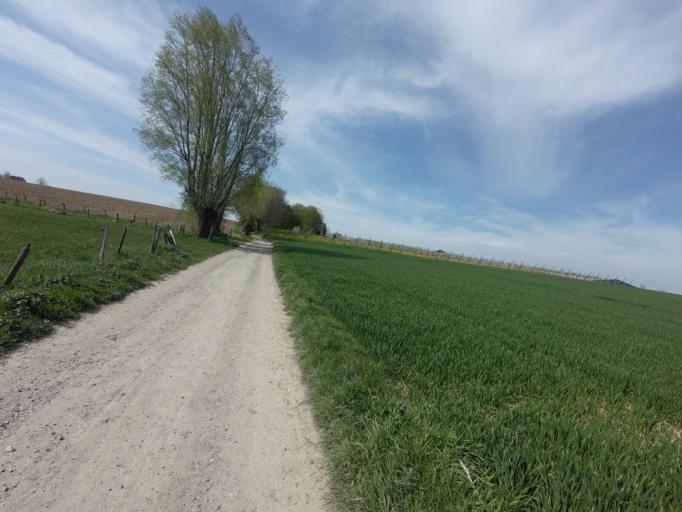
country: NL
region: Limburg
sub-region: Eijsden-Margraten
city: Margraten
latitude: 50.7938
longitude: 5.8242
